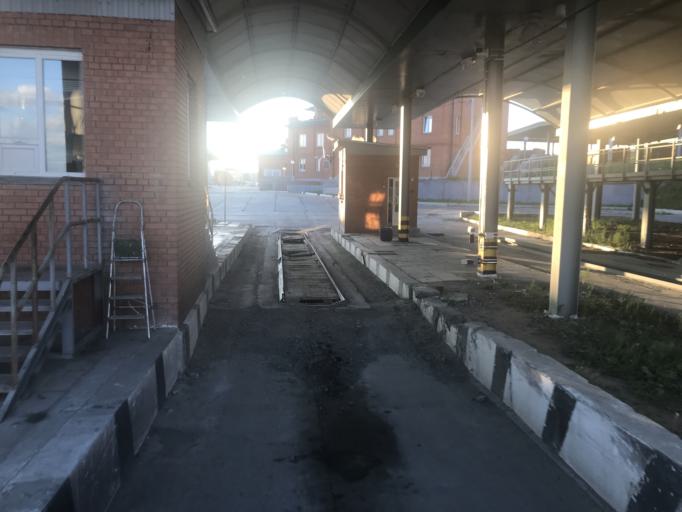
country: MN
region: Selenge
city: Altanbulag
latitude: 50.3252
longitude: 106.4876
